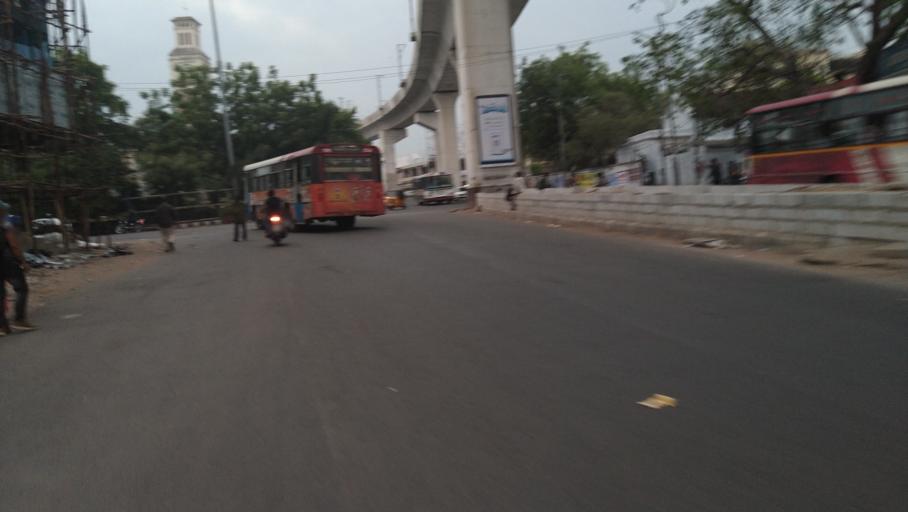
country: IN
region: Telangana
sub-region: Hyderabad
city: Malkajgiri
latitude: 17.4401
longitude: 78.4988
